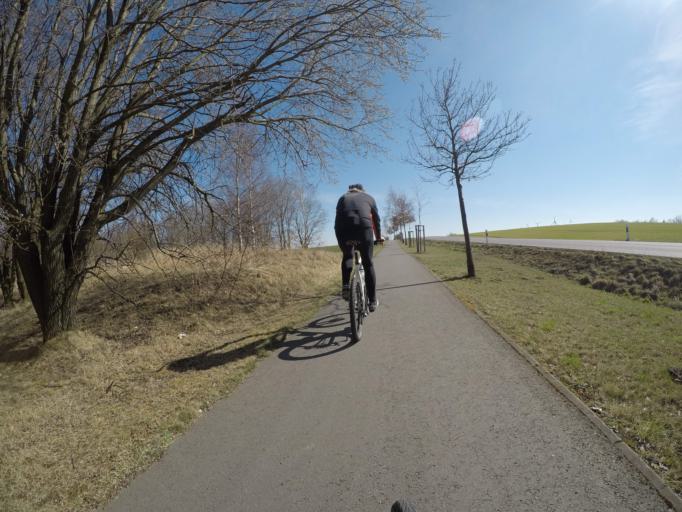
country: DE
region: Saxony
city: Freiberg
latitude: 50.9007
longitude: 13.3664
